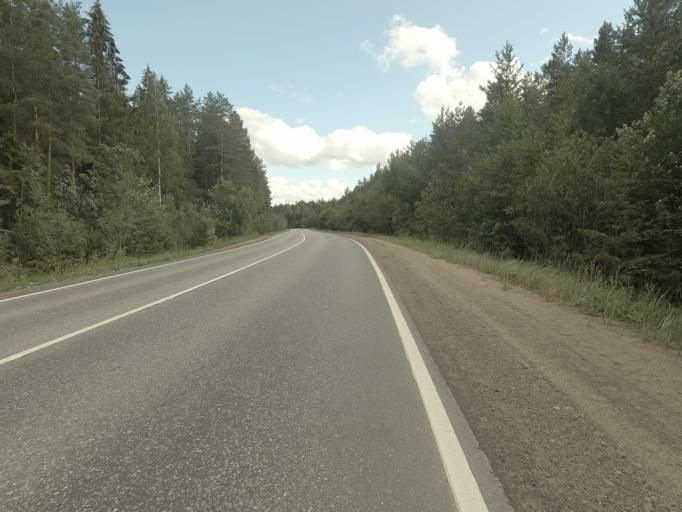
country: RU
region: Leningrad
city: Shcheglovo
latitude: 60.0129
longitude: 30.8541
